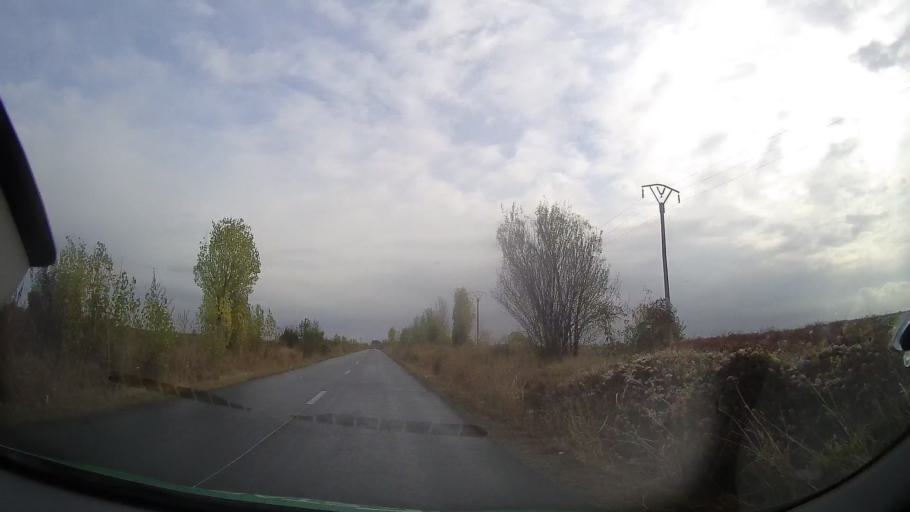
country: RO
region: Ialomita
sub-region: Comuna Maia
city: Maia
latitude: 44.7507
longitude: 26.3904
